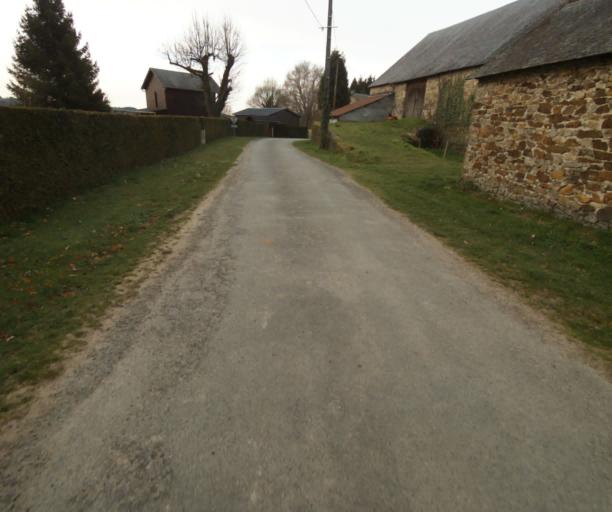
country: FR
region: Limousin
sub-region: Departement de la Correze
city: Correze
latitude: 45.4341
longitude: 1.8207
